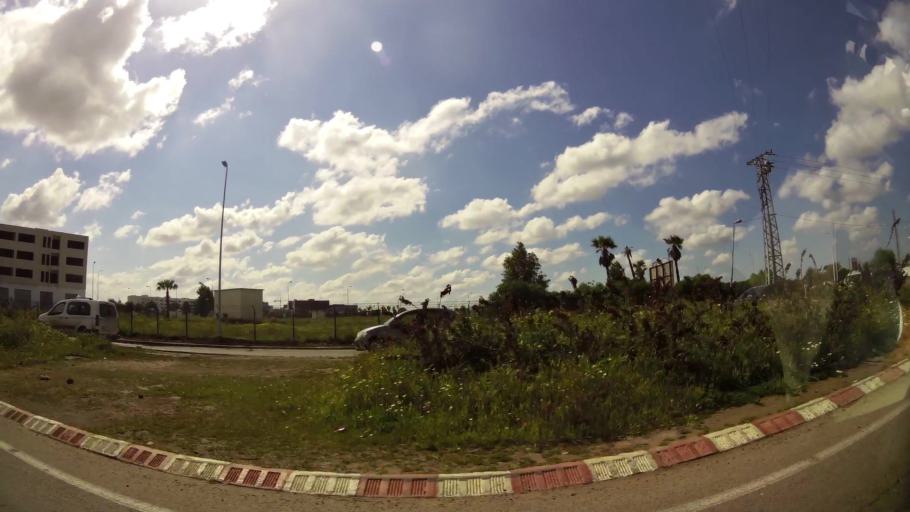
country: MA
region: Grand Casablanca
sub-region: Mediouna
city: Mediouna
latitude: 33.4090
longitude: -7.5332
